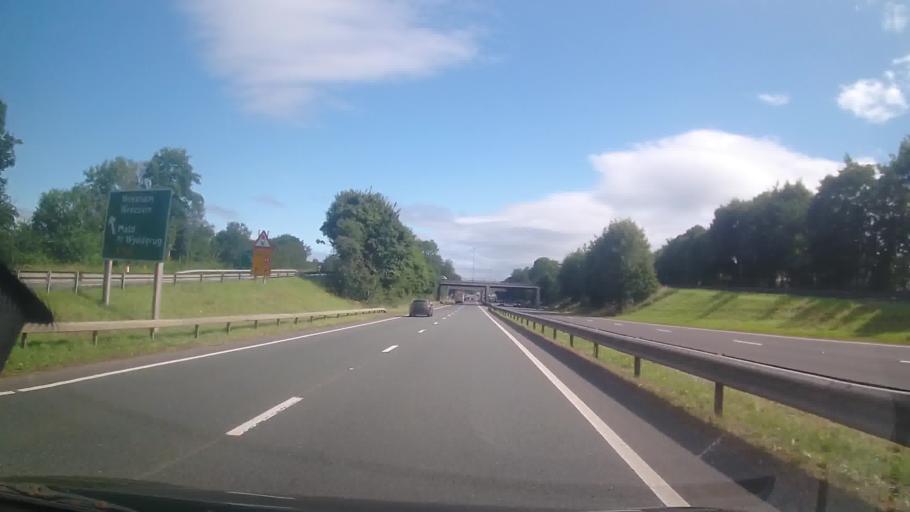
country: GB
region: Wales
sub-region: Wrexham
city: Wrexham
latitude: 53.0532
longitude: -3.0137
